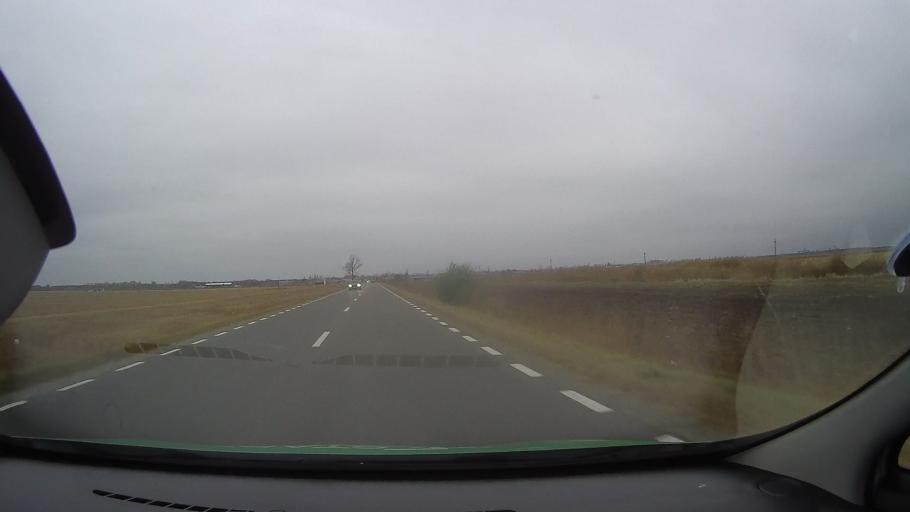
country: RO
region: Ialomita
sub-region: Comuna Slobozia
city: Slobozia
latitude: 44.5884
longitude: 27.3897
